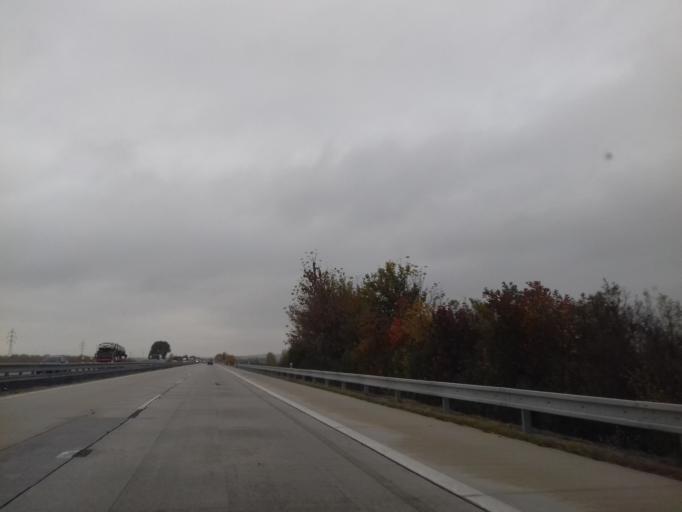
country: CZ
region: South Moravian
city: Podivin
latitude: 48.8542
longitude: 16.8439
